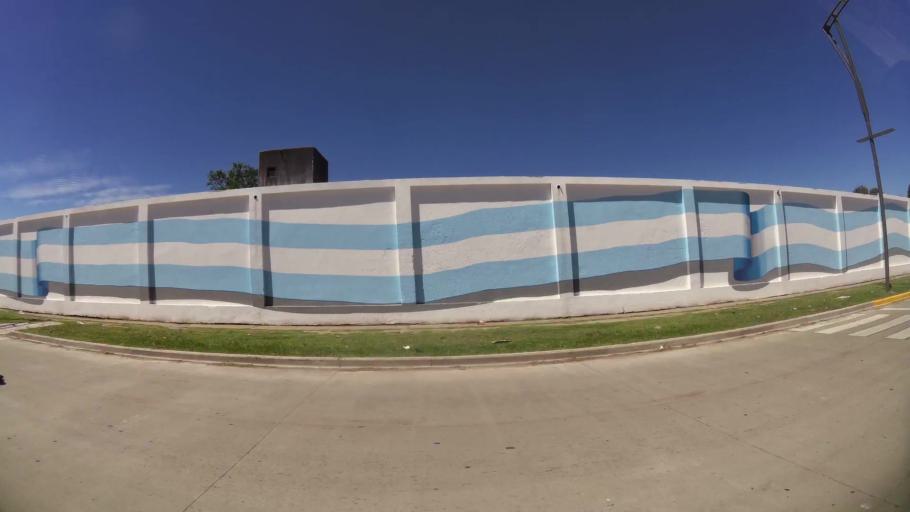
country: AR
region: Santa Fe
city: Perez
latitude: -32.9595
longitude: -60.7130
